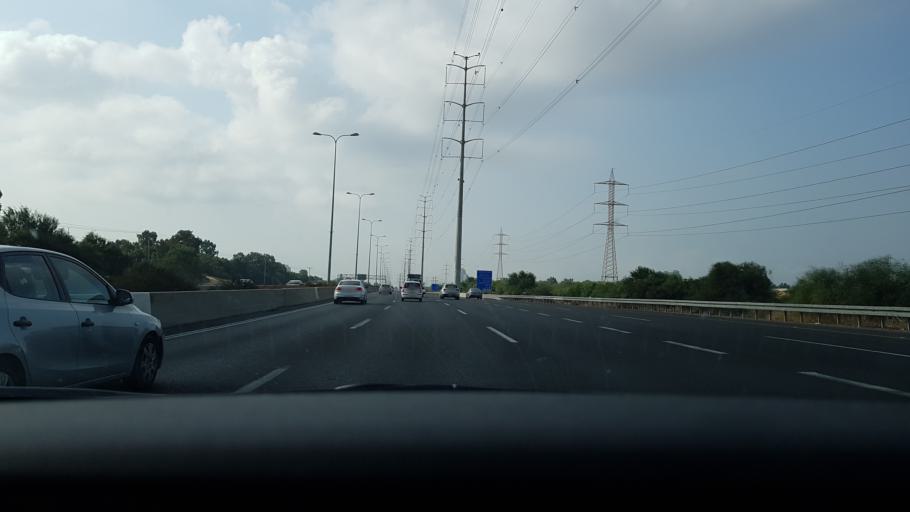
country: IL
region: Central District
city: Bet Dagan
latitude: 31.9953
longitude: 34.7999
